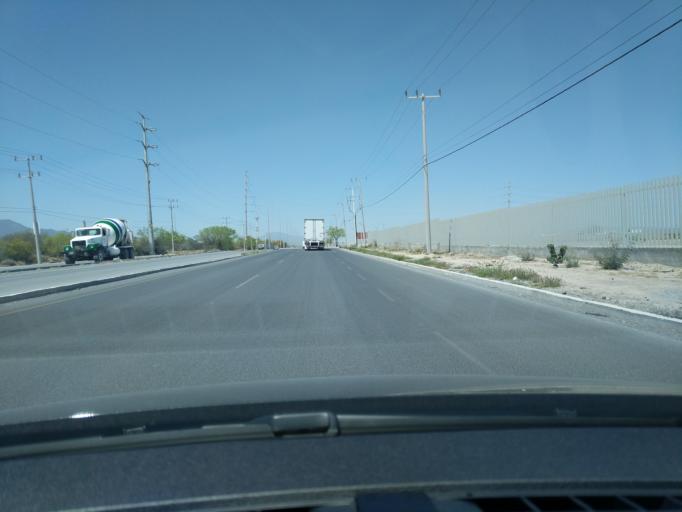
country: MX
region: Nuevo Leon
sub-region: Salinas Victoria
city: Emiliano Zapata
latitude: 25.8983
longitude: -100.2617
